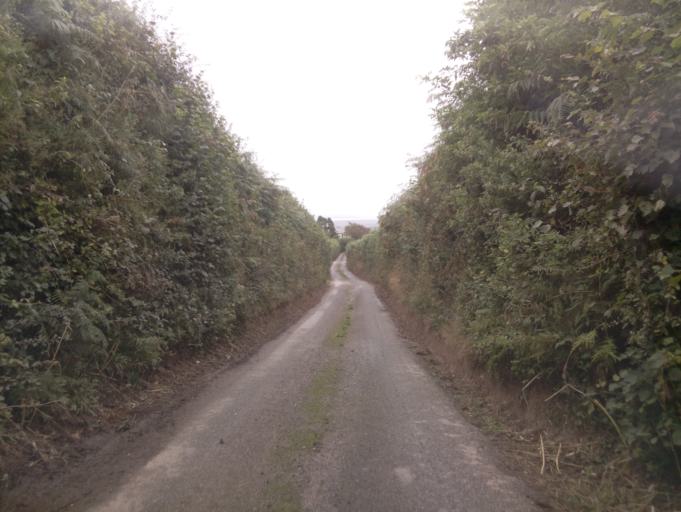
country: GB
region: England
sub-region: Devon
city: Kingsbridge
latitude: 50.2979
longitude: -3.7166
